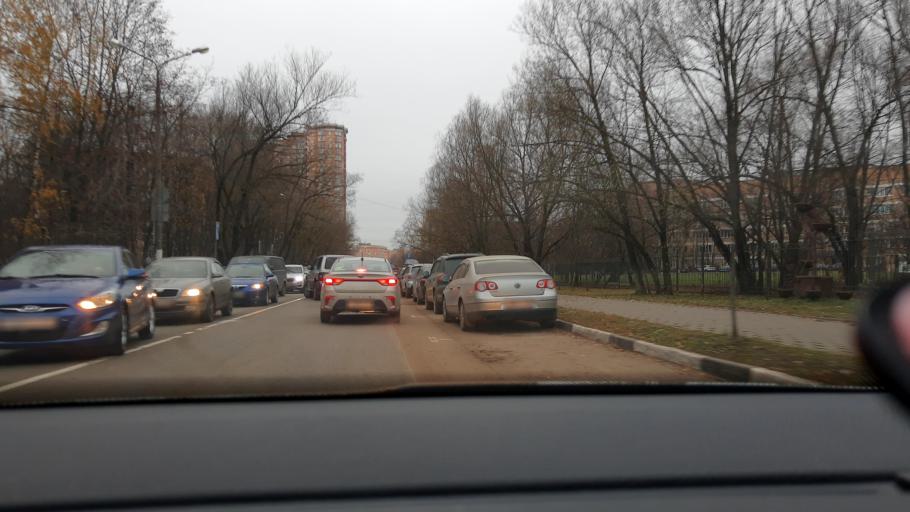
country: RU
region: Moskovskaya
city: Odintsovo
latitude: 55.6842
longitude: 37.2639
